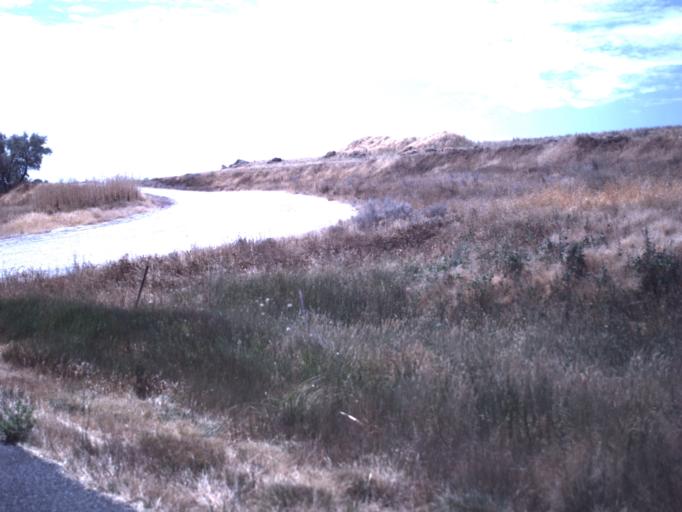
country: US
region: Utah
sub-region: Box Elder County
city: Tremonton
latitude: 41.6644
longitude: -112.2965
